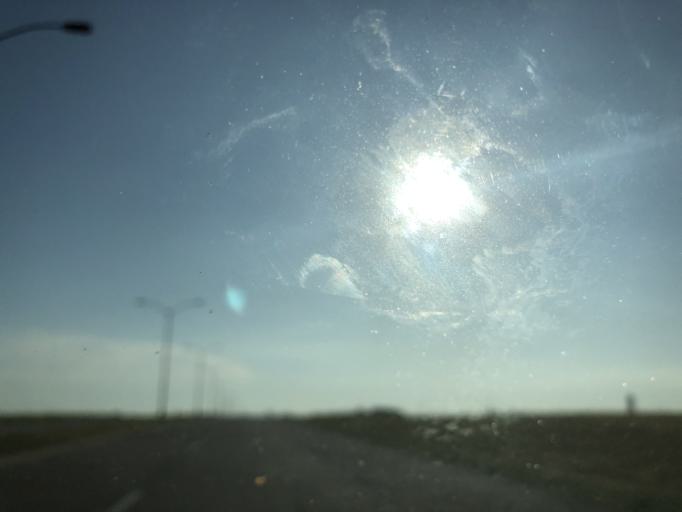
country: US
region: Texas
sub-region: Tarrant County
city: Grapevine
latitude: 32.9246
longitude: -97.0535
